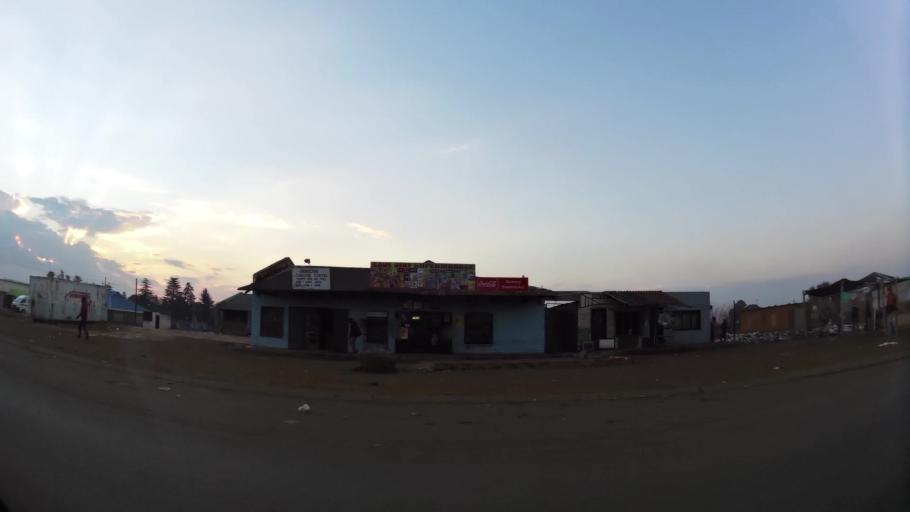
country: ZA
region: Gauteng
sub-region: City of Johannesburg Metropolitan Municipality
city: Orange Farm
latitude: -26.5487
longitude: 27.8752
